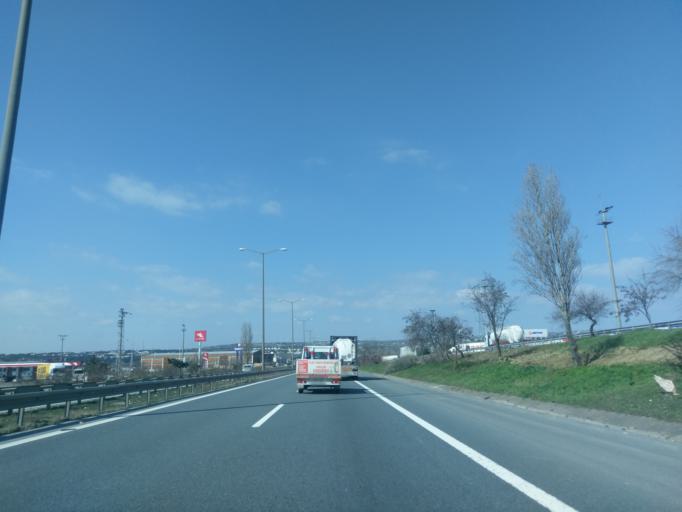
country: TR
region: Istanbul
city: Ortakoy
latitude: 41.0824
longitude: 28.3702
